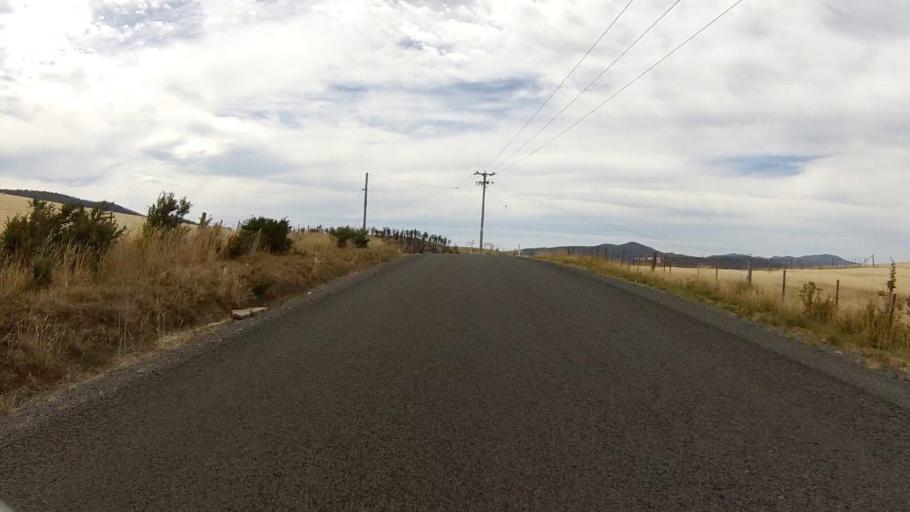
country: AU
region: Tasmania
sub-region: Sorell
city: Sorell
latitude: -42.8996
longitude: 147.7652
